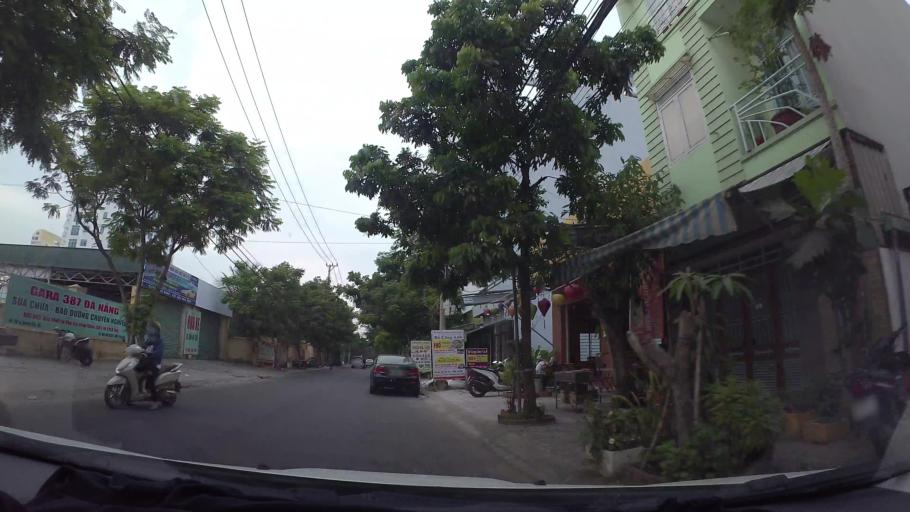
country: VN
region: Da Nang
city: Son Tra
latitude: 16.0538
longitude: 108.2444
